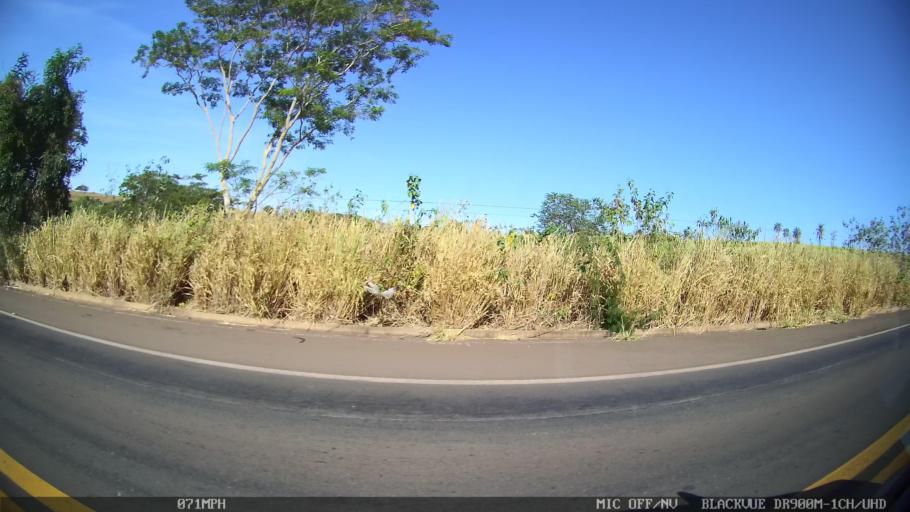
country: BR
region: Sao Paulo
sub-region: Olimpia
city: Olimpia
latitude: -20.6342
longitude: -48.8167
